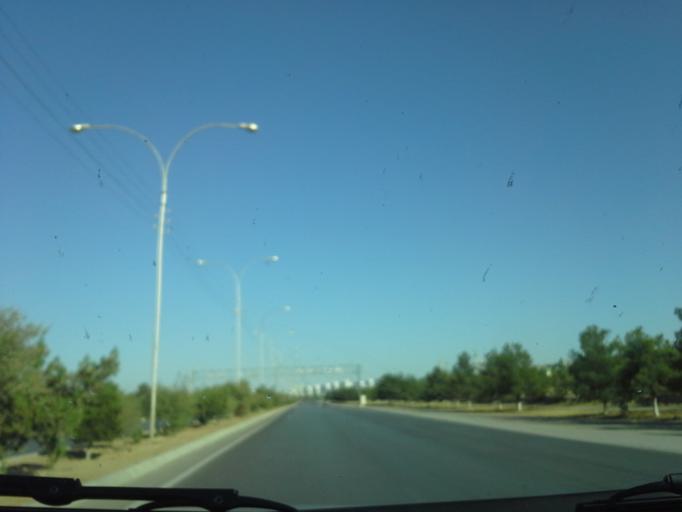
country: TM
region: Ahal
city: Ashgabat
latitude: 37.9646
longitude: 58.3081
